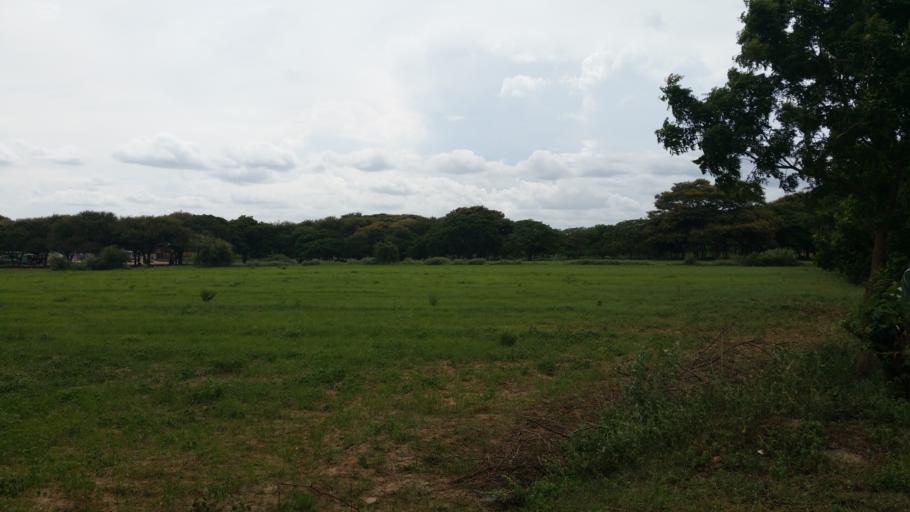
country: MM
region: Magway
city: Pakokku
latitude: 21.1644
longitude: 94.8748
